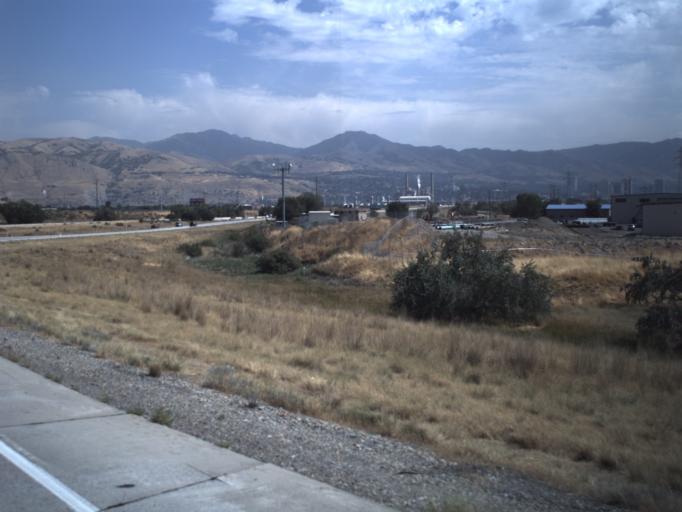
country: US
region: Utah
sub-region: Salt Lake County
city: Salt Lake City
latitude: 40.7631
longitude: -111.9491
